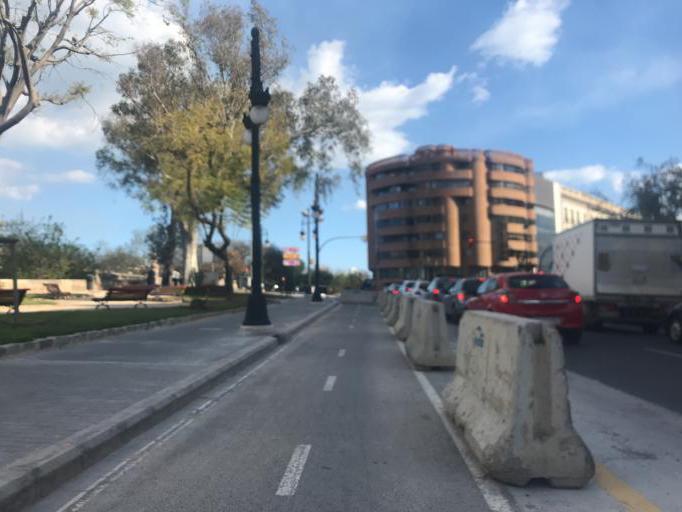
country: ES
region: Valencia
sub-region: Provincia de Valencia
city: Valencia
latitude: 39.4762
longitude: -0.3701
